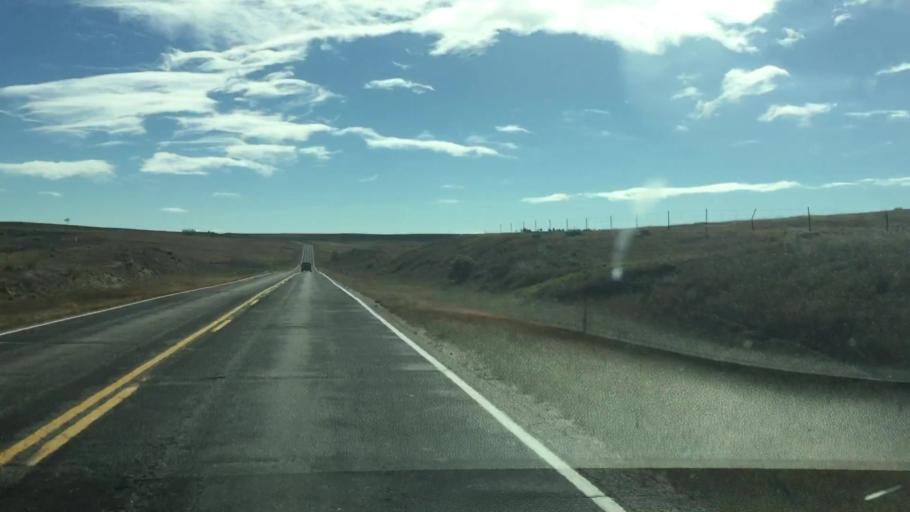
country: US
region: Colorado
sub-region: Elbert County
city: Kiowa
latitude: 39.2770
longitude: -104.2635
